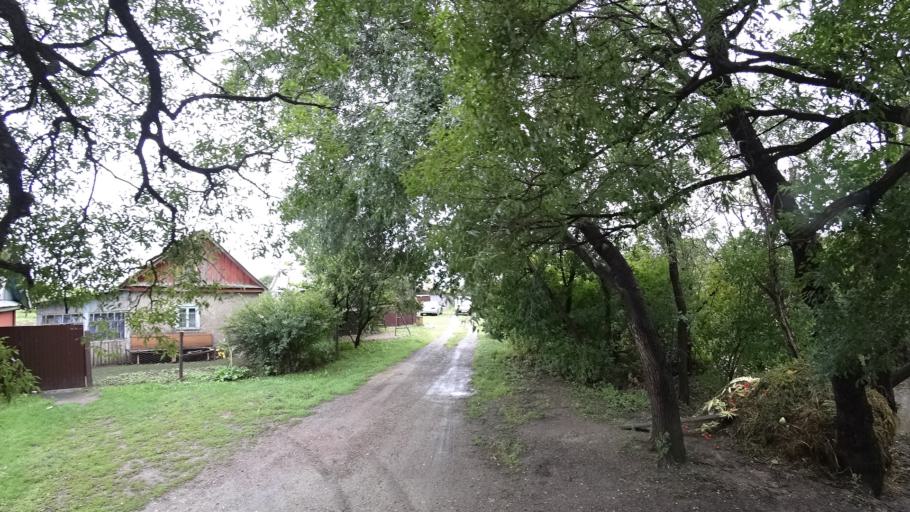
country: RU
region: Primorskiy
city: Monastyrishche
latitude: 44.2054
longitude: 132.4222
